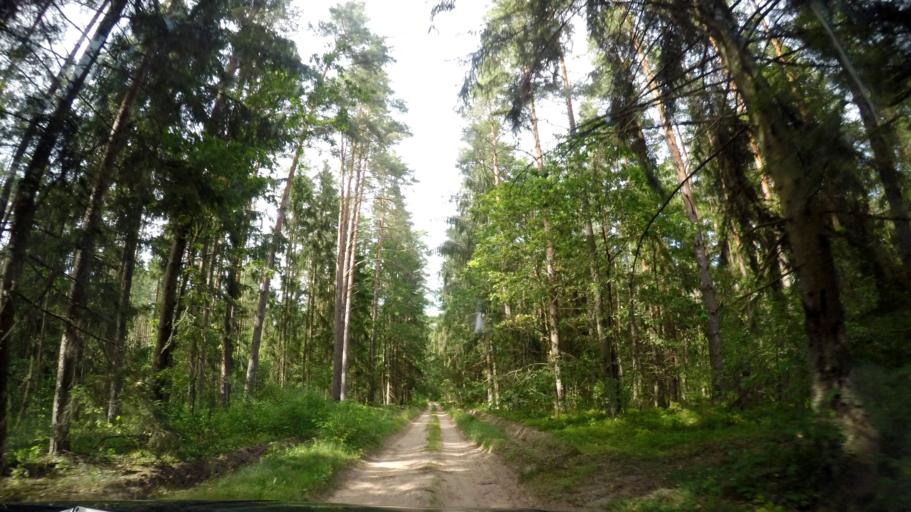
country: BY
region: Grodnenskaya
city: Skidal'
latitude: 53.8318
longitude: 24.1772
